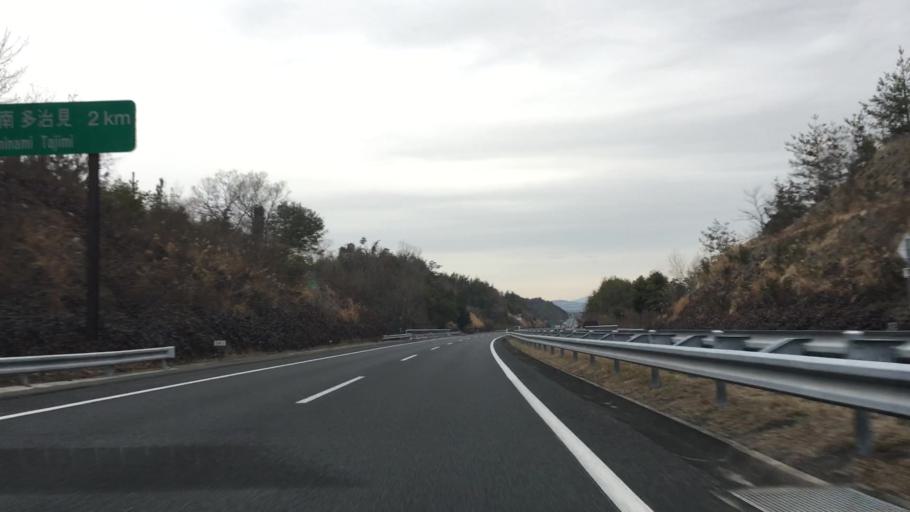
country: JP
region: Gifu
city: Toki
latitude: 35.3133
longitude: 137.1772
